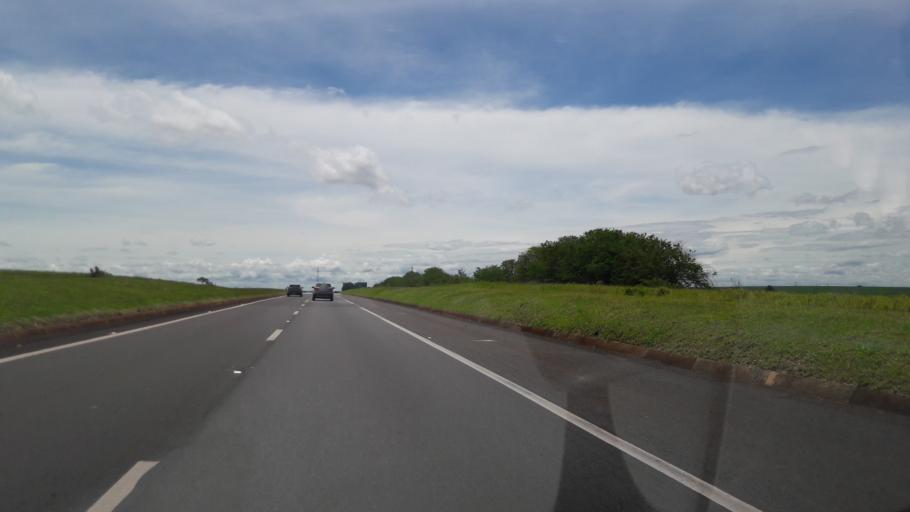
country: BR
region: Sao Paulo
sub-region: Avare
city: Avare
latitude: -22.9566
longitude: -48.8452
